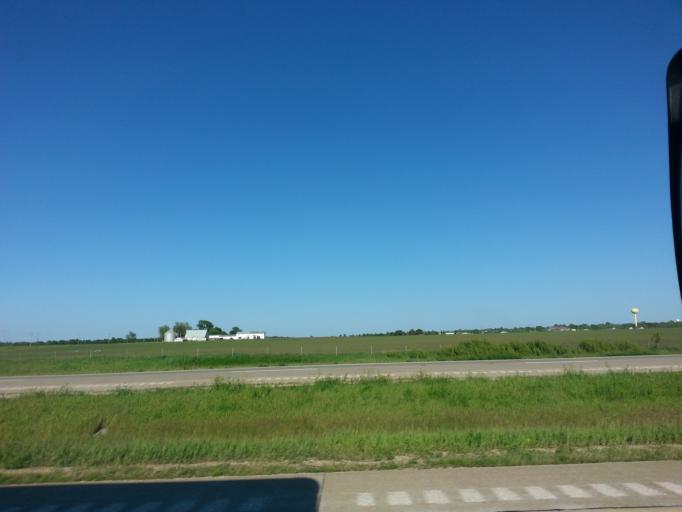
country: US
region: Illinois
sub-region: Woodford County
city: El Paso
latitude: 40.7501
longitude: -89.0348
